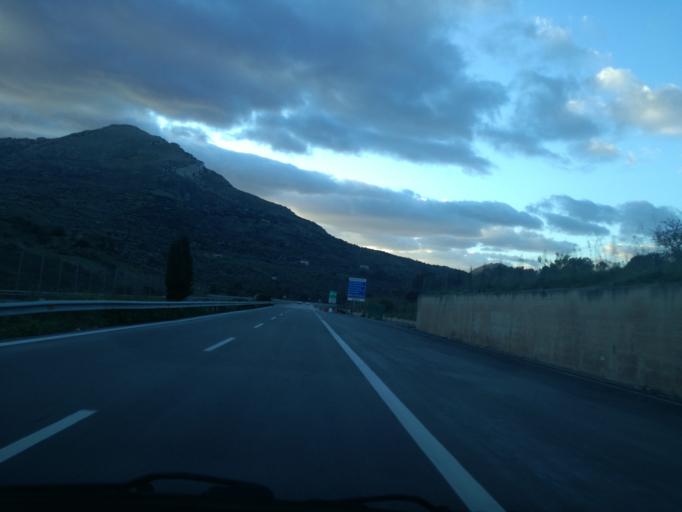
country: IT
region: Sicily
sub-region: Palermo
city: Scillato
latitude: 37.8359
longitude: 13.9341
